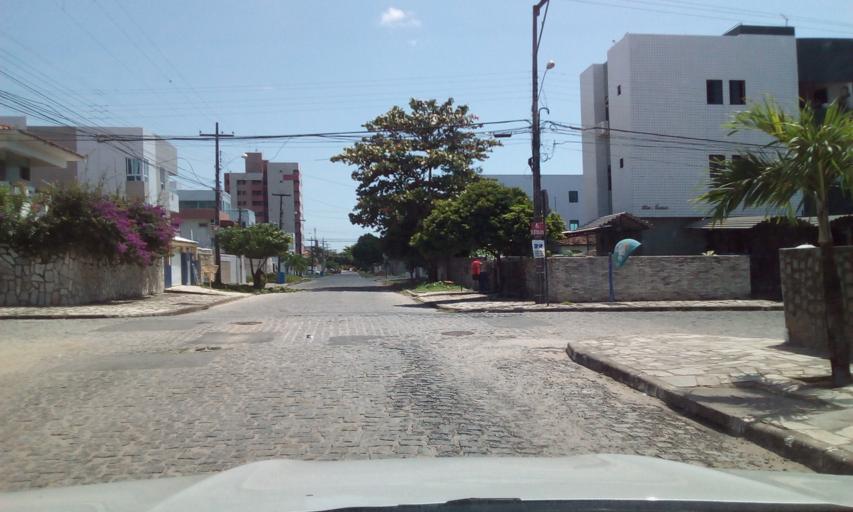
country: BR
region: Paraiba
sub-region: Joao Pessoa
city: Joao Pessoa
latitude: -7.0682
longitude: -34.8415
